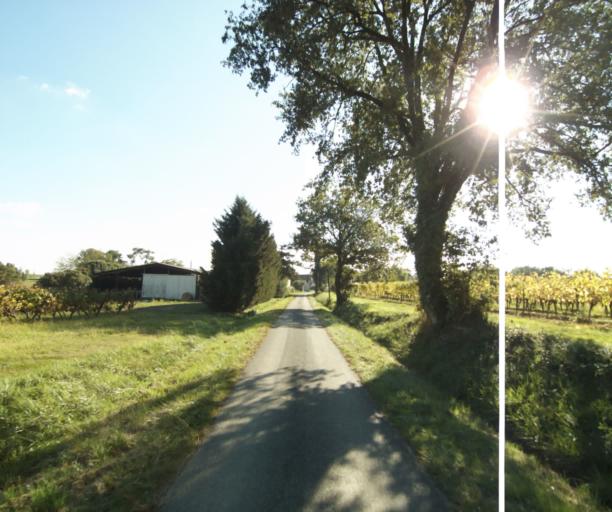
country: FR
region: Midi-Pyrenees
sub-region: Departement du Gers
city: Eauze
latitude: 43.8007
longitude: 0.1283
